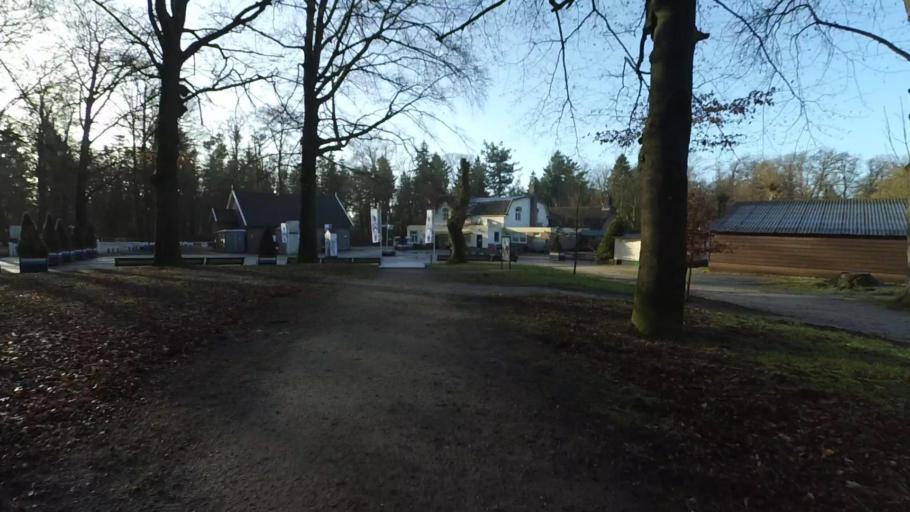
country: NL
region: Utrecht
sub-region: Gemeente Utrechtse Heuvelrug
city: Maarn
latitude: 52.0875
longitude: 5.3391
